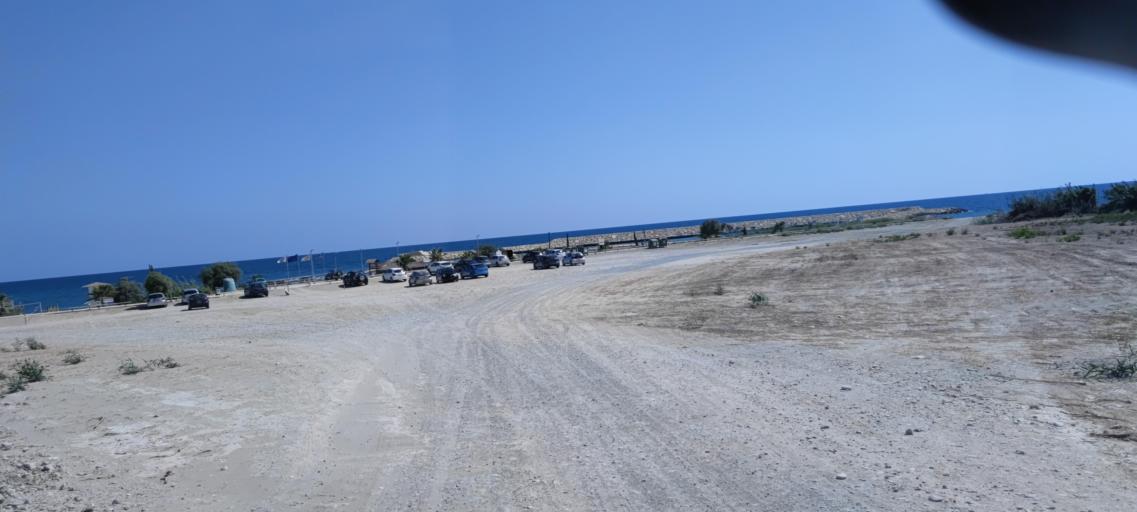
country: CY
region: Larnaka
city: Kofinou
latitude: 34.7759
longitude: 33.4687
